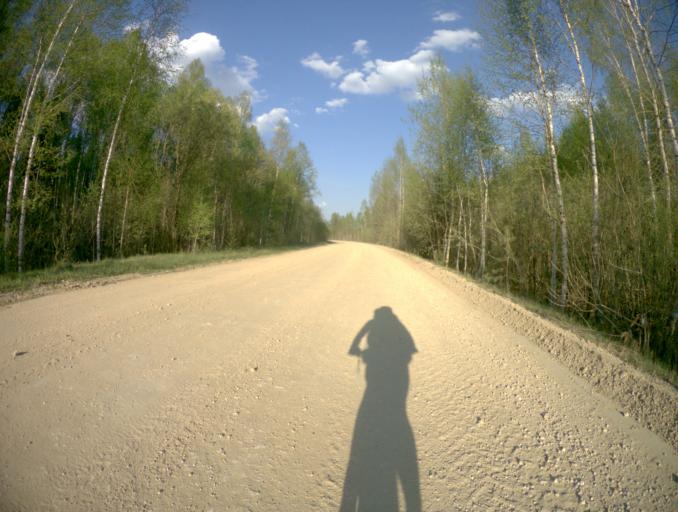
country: RU
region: Vladimir
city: Mstera
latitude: 56.5505
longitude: 41.7995
